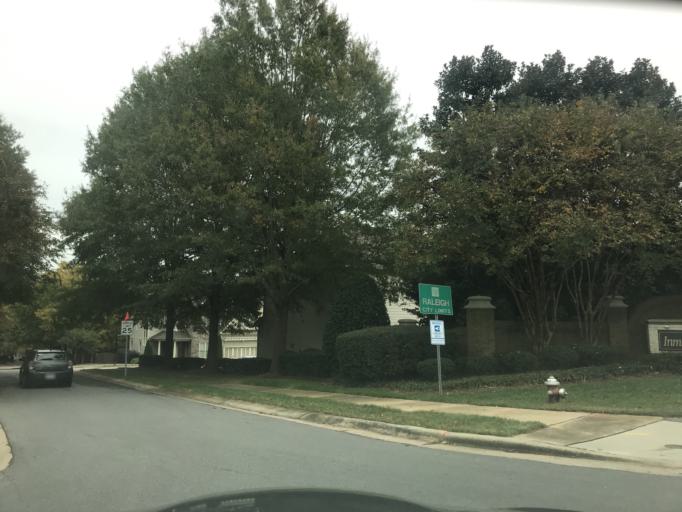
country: US
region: North Carolina
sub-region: Wake County
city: West Raleigh
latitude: 35.8451
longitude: -78.6739
